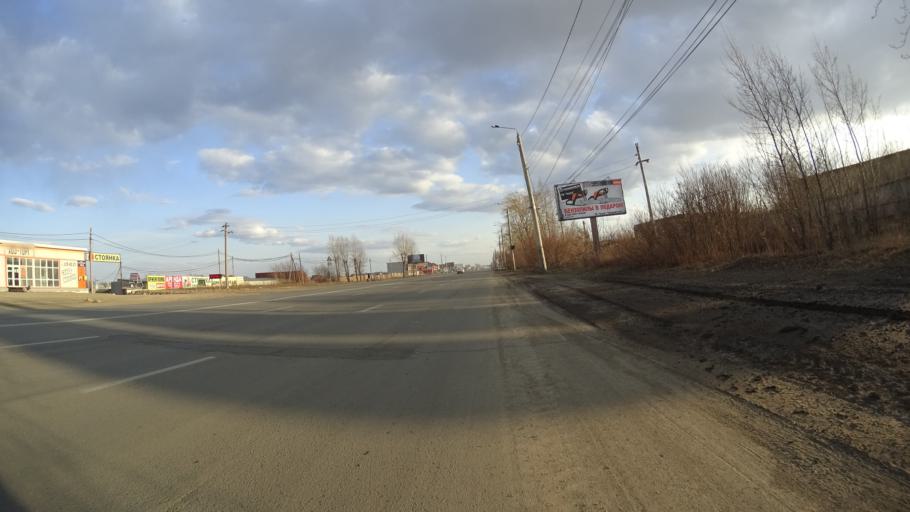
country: RU
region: Chelyabinsk
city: Novosineglazovskiy
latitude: 55.0971
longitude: 61.3877
